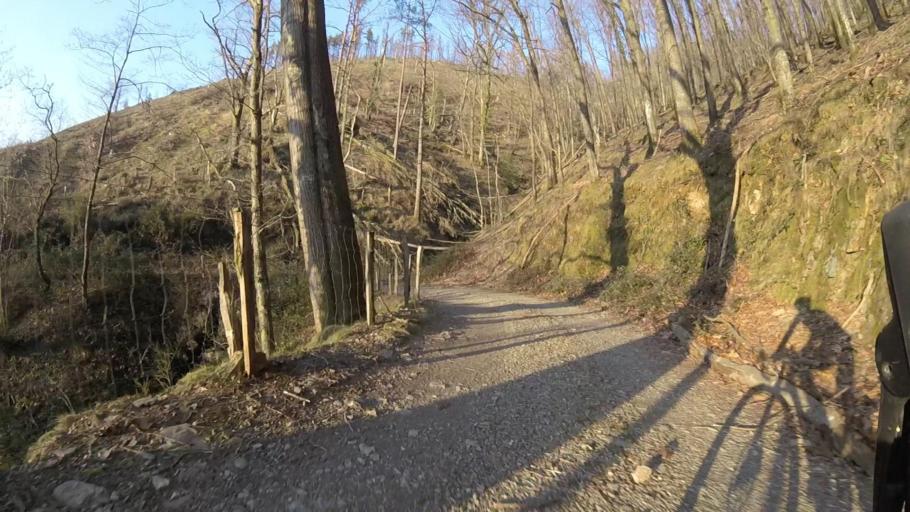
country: ES
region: Navarre
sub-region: Provincia de Navarra
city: Arano
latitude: 43.2480
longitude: -1.8563
